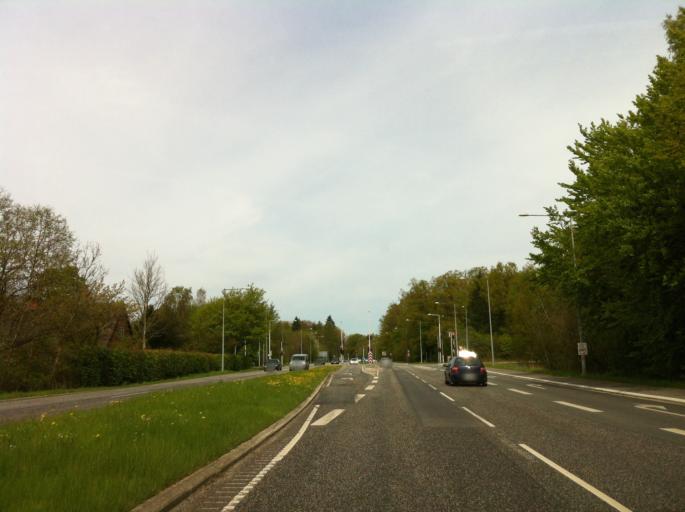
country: DK
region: Capital Region
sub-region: Hillerod Kommune
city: Hillerod
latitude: 55.9189
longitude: 12.3340
